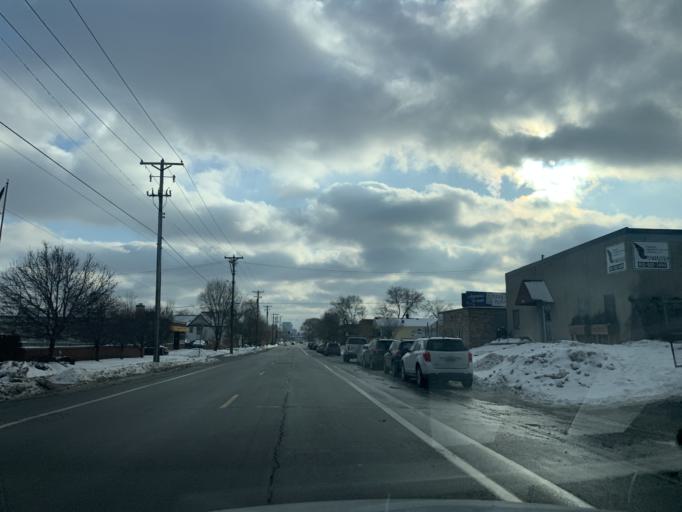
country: US
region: Minnesota
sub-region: Anoka County
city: Columbia Heights
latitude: 45.0155
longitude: -93.2810
